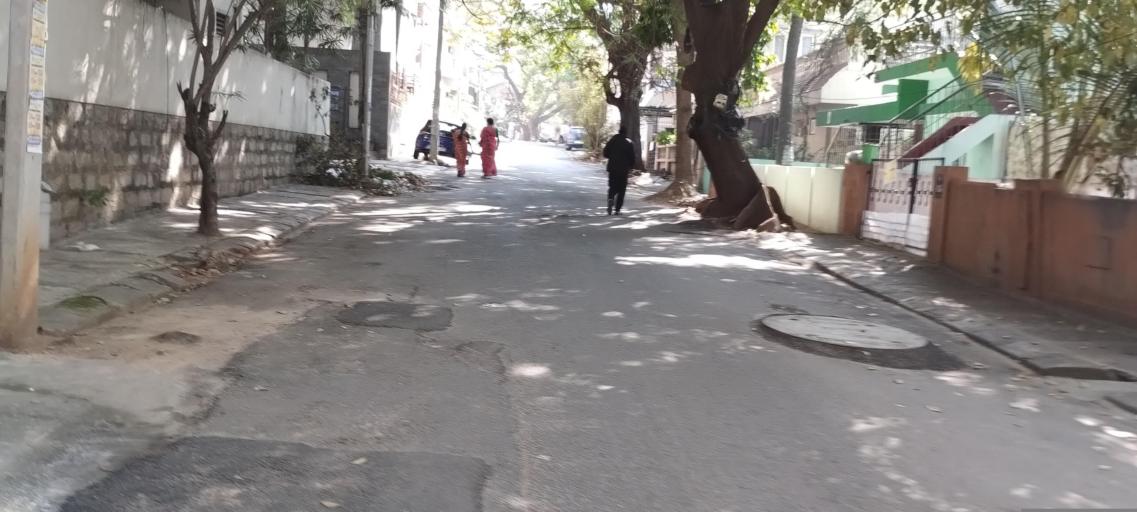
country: IN
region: Karnataka
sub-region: Bangalore Urban
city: Bangalore
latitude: 12.9345
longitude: 77.5407
